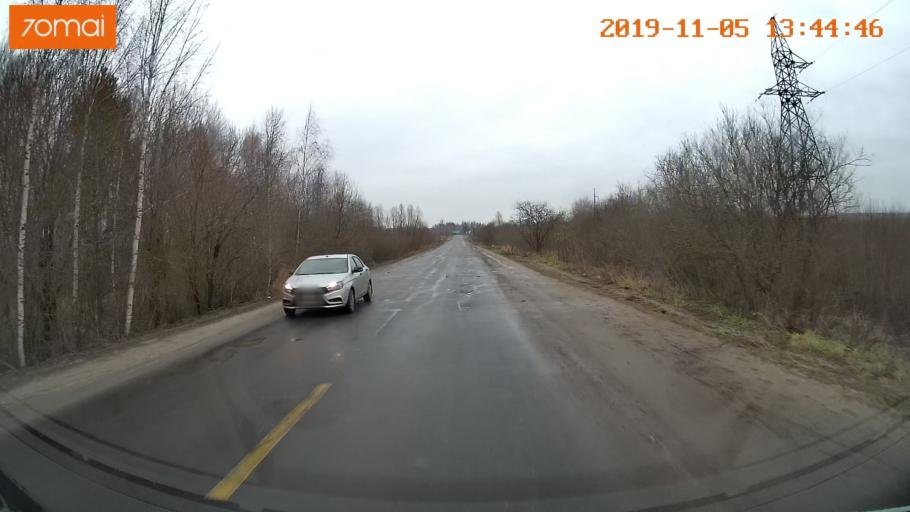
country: RU
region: Ivanovo
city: Shuya
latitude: 56.9834
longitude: 41.4114
